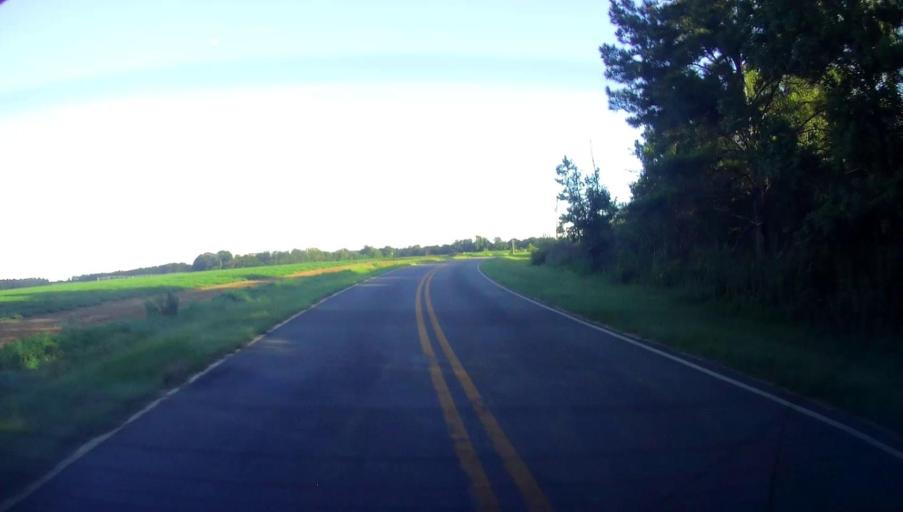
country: US
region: Georgia
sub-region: Pulaski County
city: Hawkinsville
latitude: 32.2822
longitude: -83.5389
